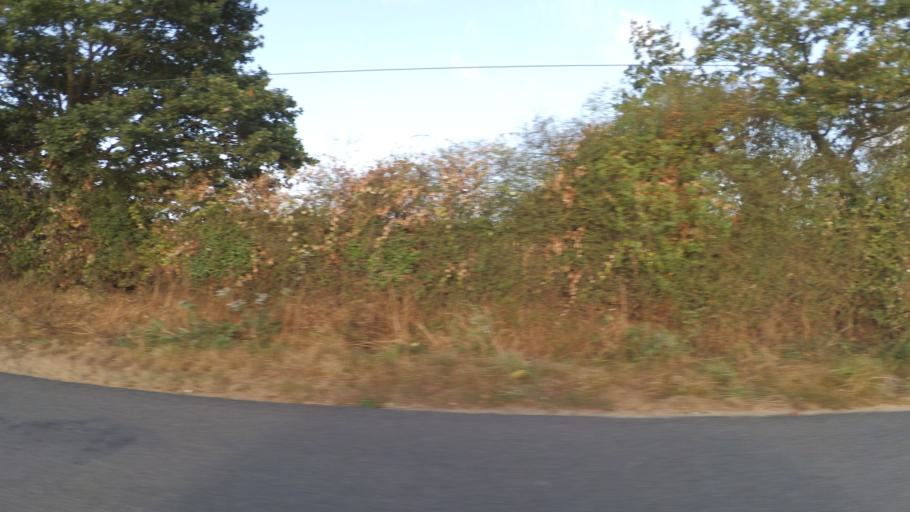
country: FR
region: Pays de la Loire
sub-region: Departement de la Loire-Atlantique
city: La Planche
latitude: 47.0038
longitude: -1.4550
